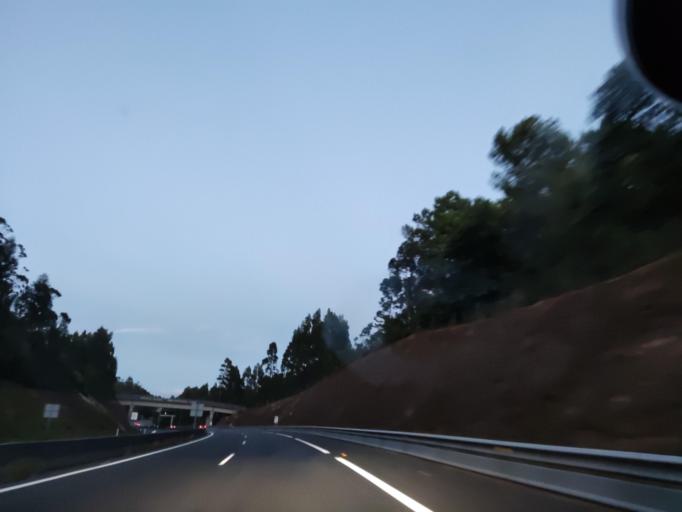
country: ES
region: Galicia
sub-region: Provincia da Coruna
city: Boiro
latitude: 42.6231
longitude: -8.9366
